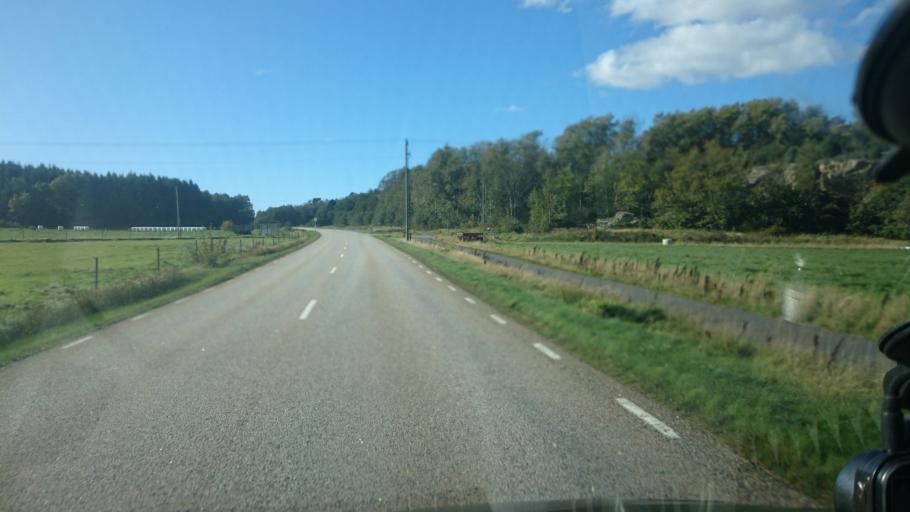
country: SE
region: Vaestra Goetaland
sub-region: Lysekils Kommun
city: Brastad
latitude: 58.3302
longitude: 11.4691
